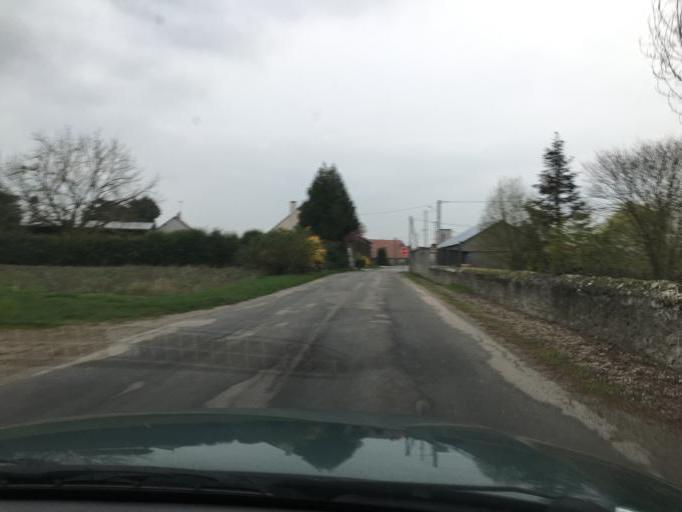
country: FR
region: Centre
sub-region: Departement du Loiret
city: Baule
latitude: 47.8194
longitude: 1.6634
